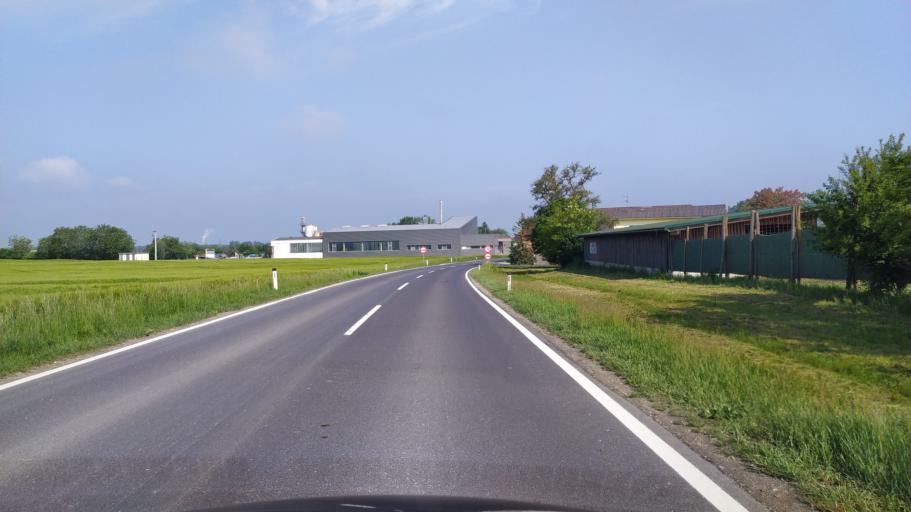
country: AT
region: Lower Austria
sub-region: Politischer Bezirk Amstetten
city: Ennsdorf
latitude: 48.2134
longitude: 14.5426
